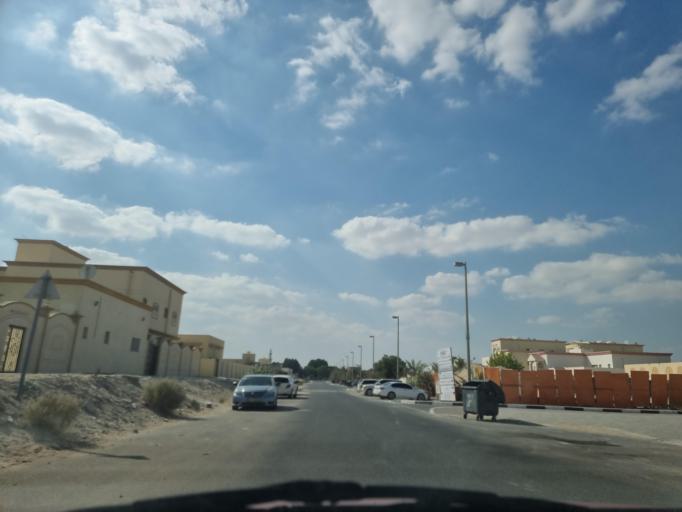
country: AE
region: Abu Dhabi
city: Abu Dhabi
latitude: 24.3999
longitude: 54.7404
